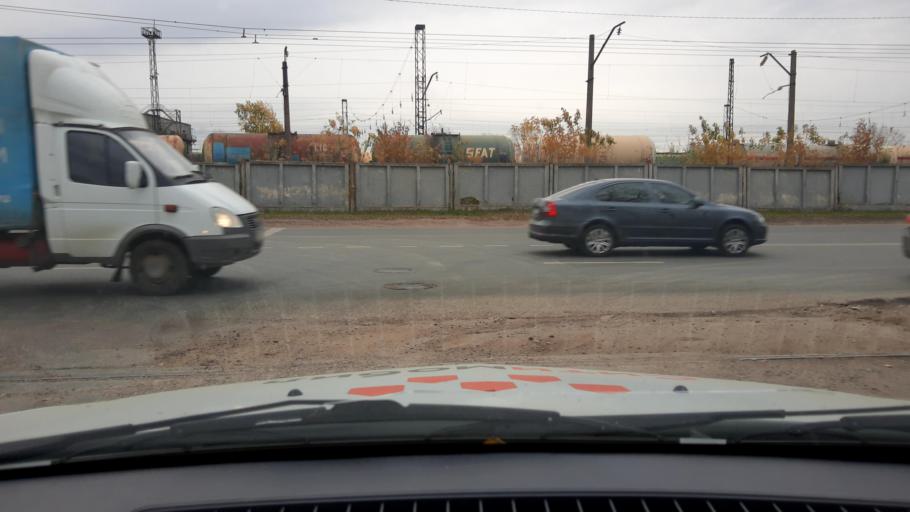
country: RU
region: Bashkortostan
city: Ufa
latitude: 54.8287
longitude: 56.0863
